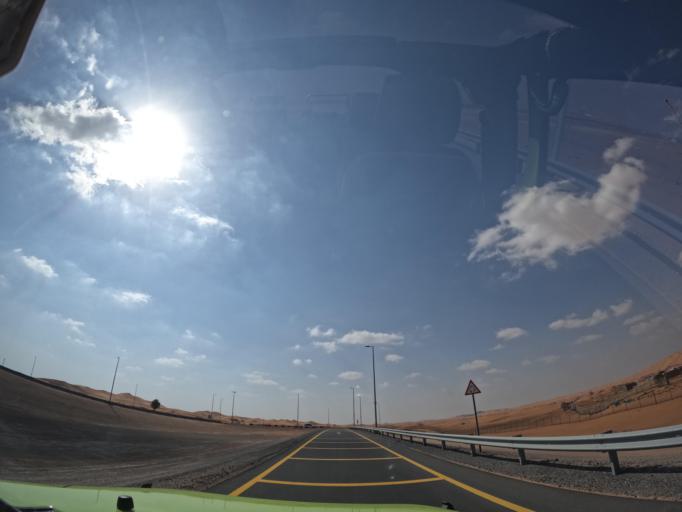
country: AE
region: Ash Shariqah
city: Adh Dhayd
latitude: 24.9422
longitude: 55.7315
